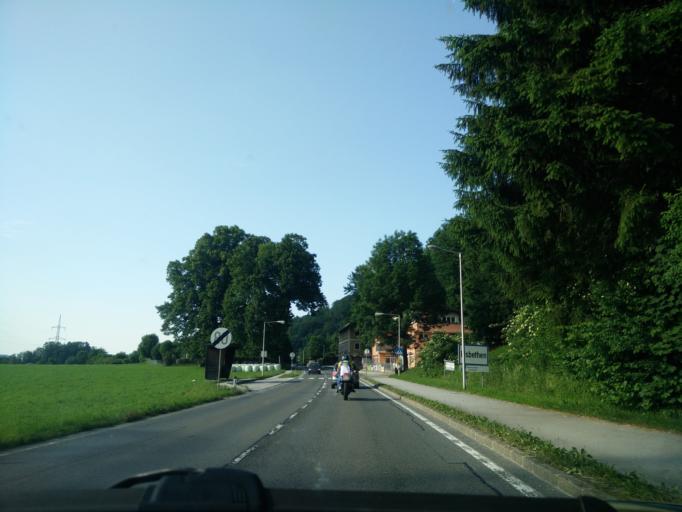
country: AT
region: Salzburg
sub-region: Politischer Bezirk Salzburg-Umgebung
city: Elsbethen
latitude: 47.7518
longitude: 13.0874
